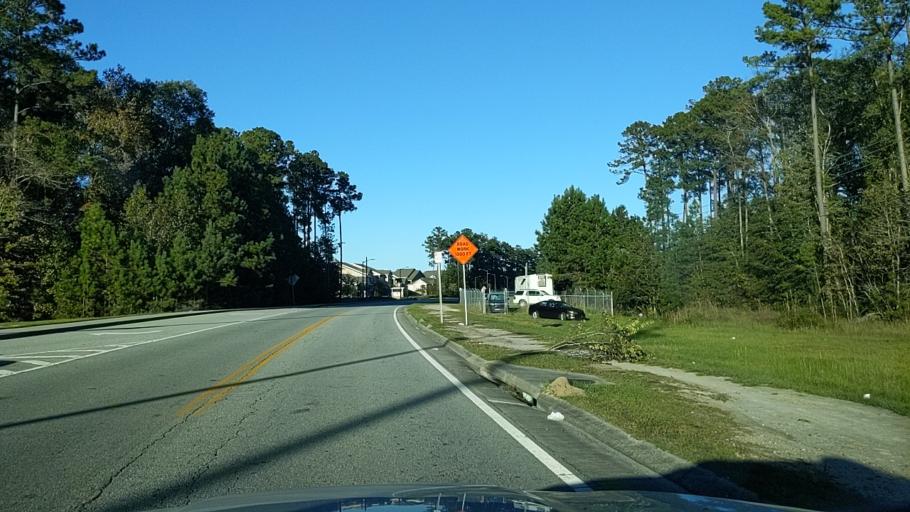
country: US
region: Georgia
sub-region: Chatham County
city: Pooler
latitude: 32.1741
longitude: -81.2329
